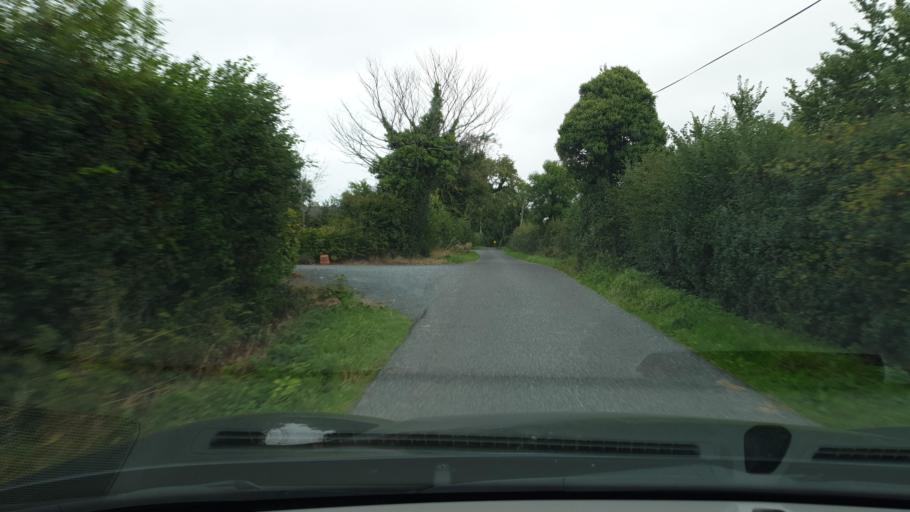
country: IE
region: Leinster
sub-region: An Mhi
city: Ratoath
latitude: 53.5215
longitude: -6.4840
